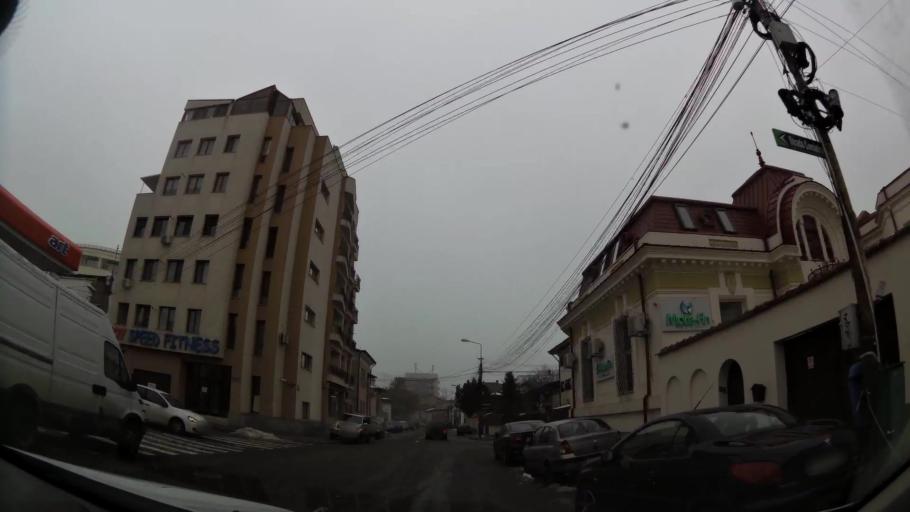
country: RO
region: Bucuresti
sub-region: Municipiul Bucuresti
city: Bucharest
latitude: 44.4479
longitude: 26.1116
